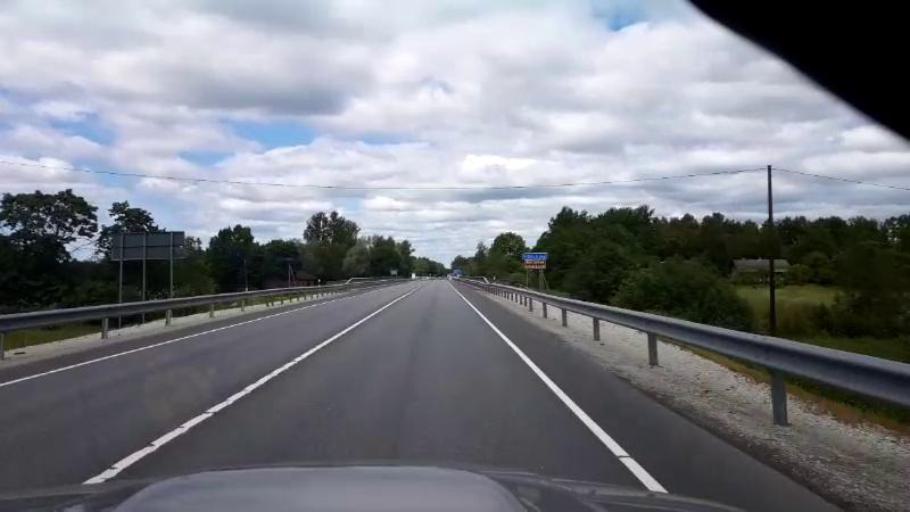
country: EE
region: Raplamaa
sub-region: Maerjamaa vald
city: Marjamaa
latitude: 58.8094
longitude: 24.4126
